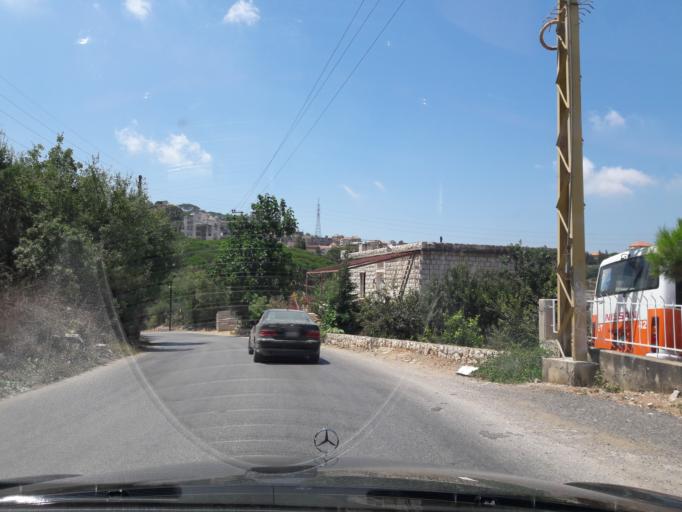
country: LB
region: Mont-Liban
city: Djounie
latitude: 33.9269
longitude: 35.6615
